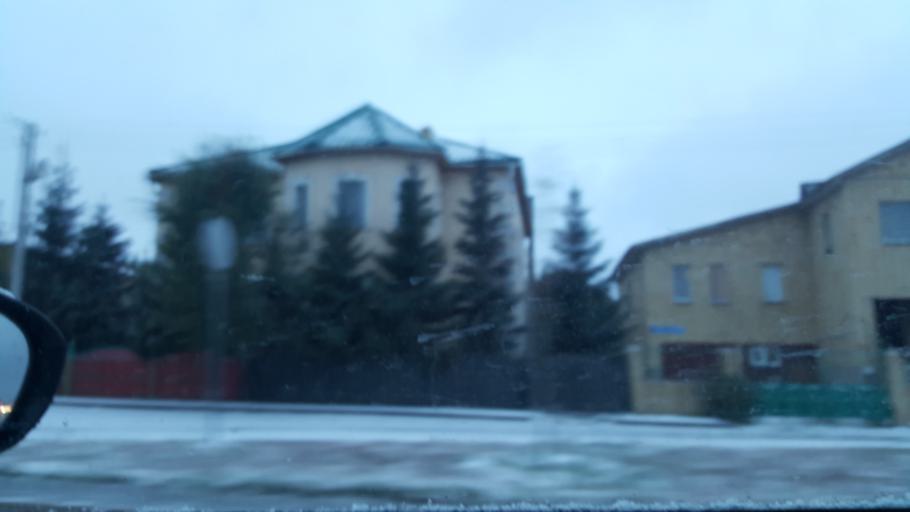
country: KZ
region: Astana Qalasy
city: Astana
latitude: 51.1382
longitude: 71.4908
